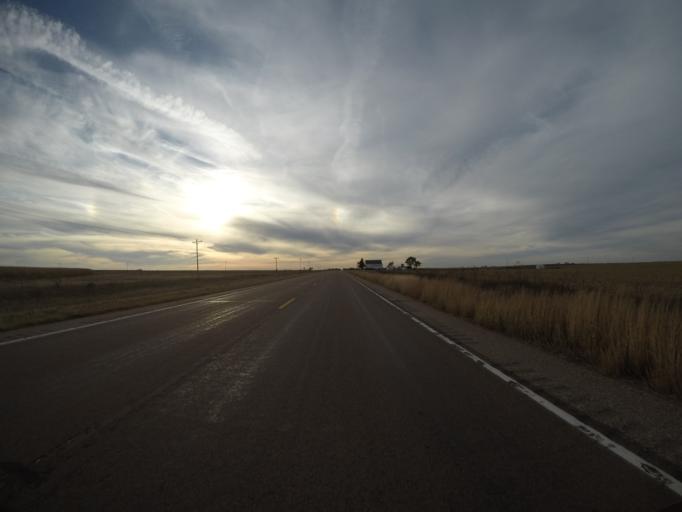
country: US
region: Colorado
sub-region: Yuma County
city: Yuma
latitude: 39.6560
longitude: -102.6467
